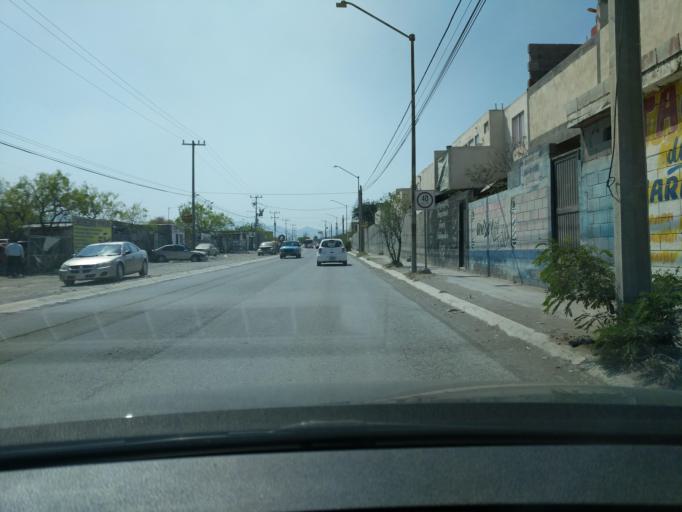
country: MX
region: Nuevo Leon
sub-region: Garcia
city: Valle de Lincoln
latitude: 25.7929
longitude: -100.4751
